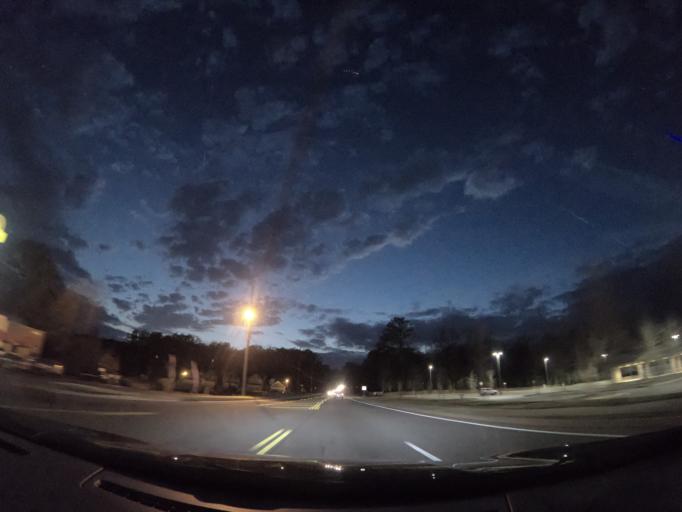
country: US
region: Georgia
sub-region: Cobb County
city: Acworth
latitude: 34.0767
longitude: -84.6562
